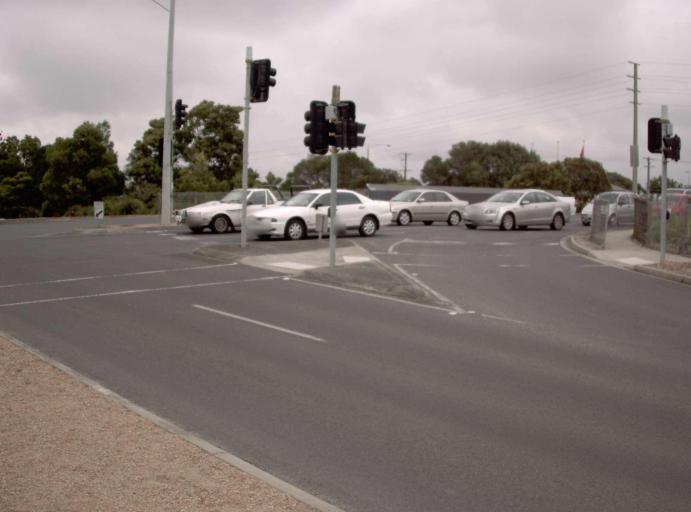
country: AU
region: Victoria
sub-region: Latrobe
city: Morwell
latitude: -38.2393
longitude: 146.4047
